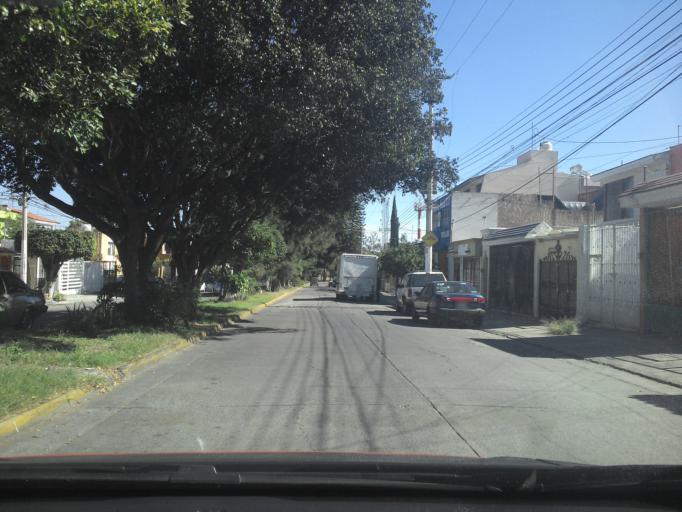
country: MX
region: Jalisco
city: Zapopan2
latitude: 20.7476
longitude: -103.4054
